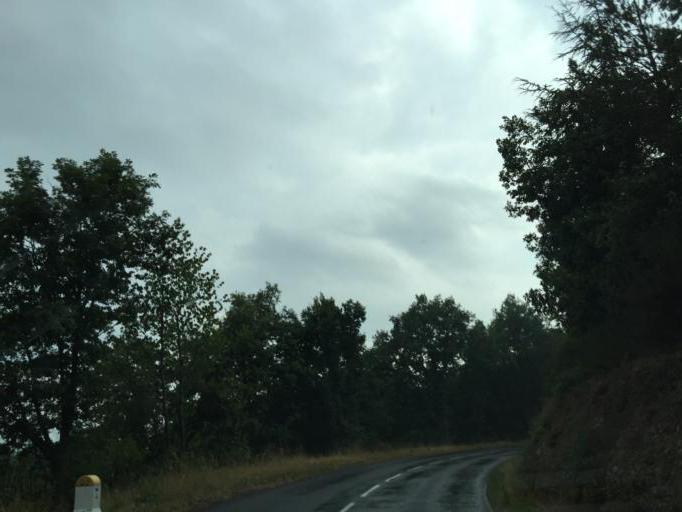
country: FR
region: Rhone-Alpes
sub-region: Departement de la Loire
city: Saint-Christo-en-Jarez
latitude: 45.5167
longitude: 4.5010
